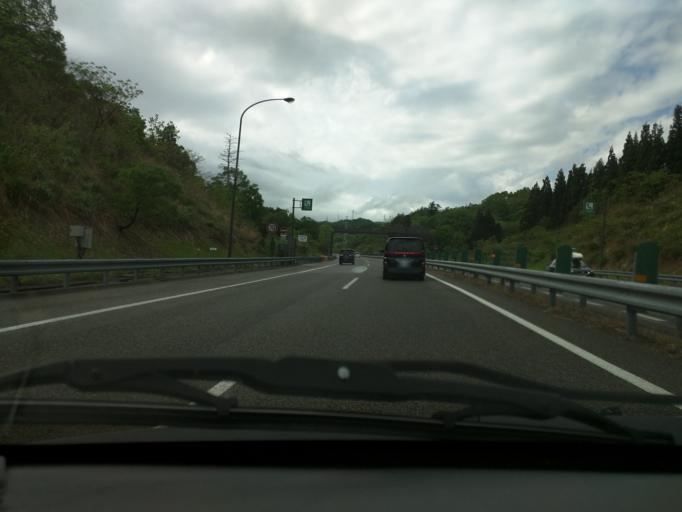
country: JP
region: Niigata
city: Joetsu
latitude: 37.1369
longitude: 138.2140
